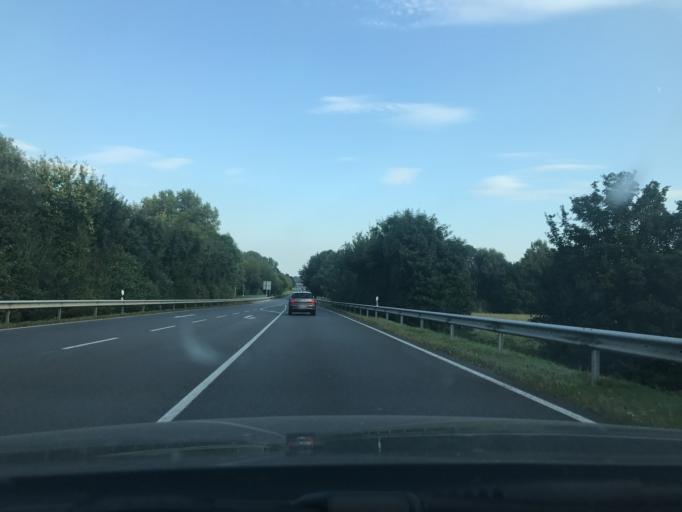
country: DE
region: North Rhine-Westphalia
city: Geldern
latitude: 51.5037
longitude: 6.3080
